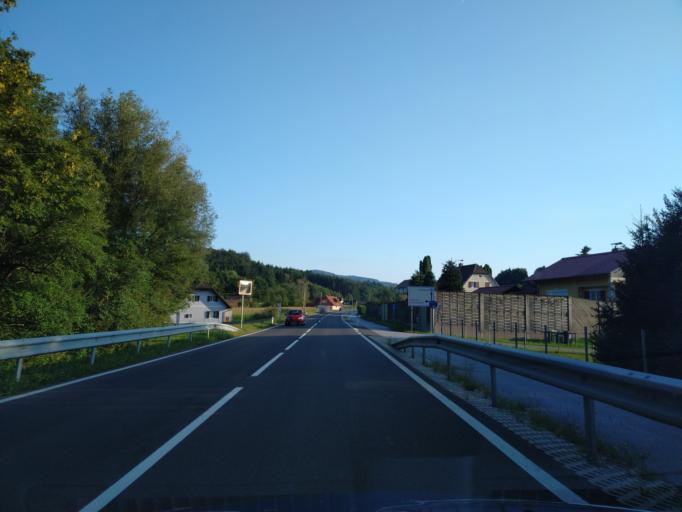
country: AT
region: Styria
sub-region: Politischer Bezirk Deutschlandsberg
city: Wies
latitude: 46.7146
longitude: 15.2529
